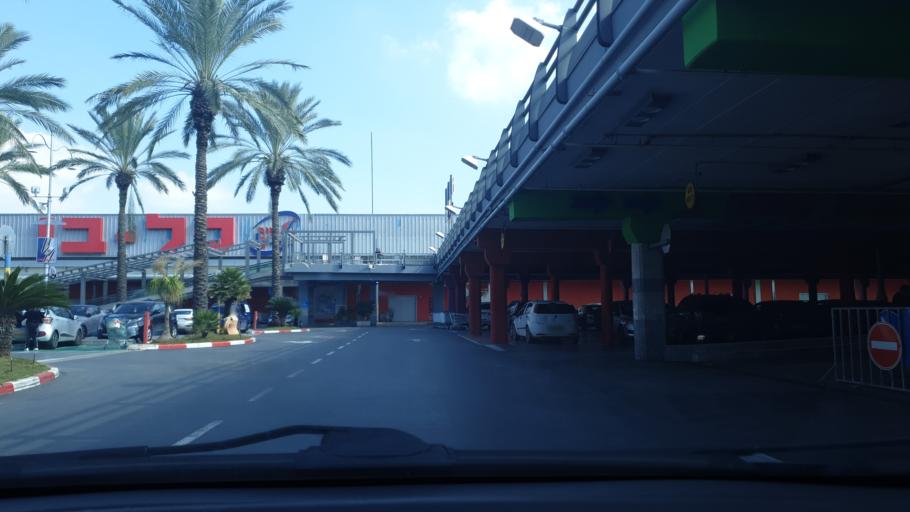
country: IL
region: Tel Aviv
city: Azor
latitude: 32.0101
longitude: 34.8086
